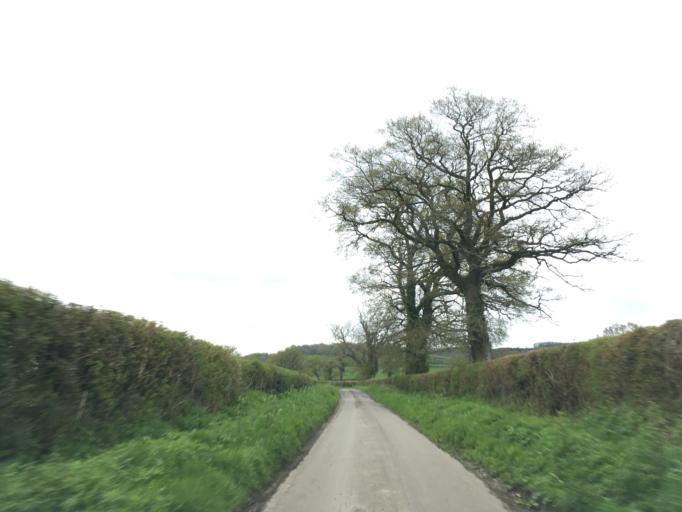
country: GB
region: England
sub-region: Gloucestershire
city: Wotton-under-Edge
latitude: 51.6232
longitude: -2.3547
